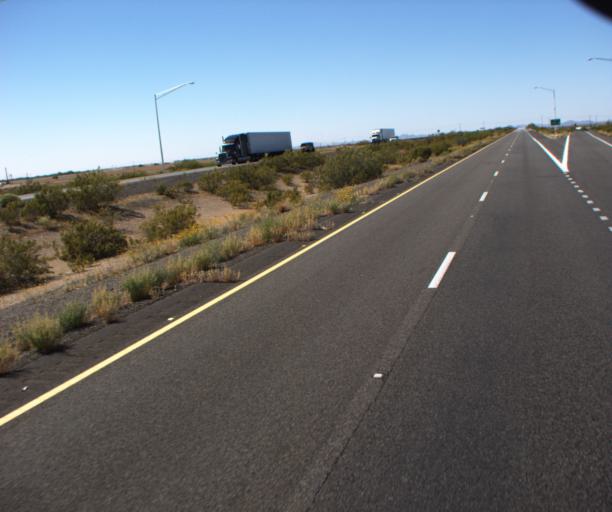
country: US
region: Arizona
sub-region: Maricopa County
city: Gila Bend
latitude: 32.9392
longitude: -112.7299
